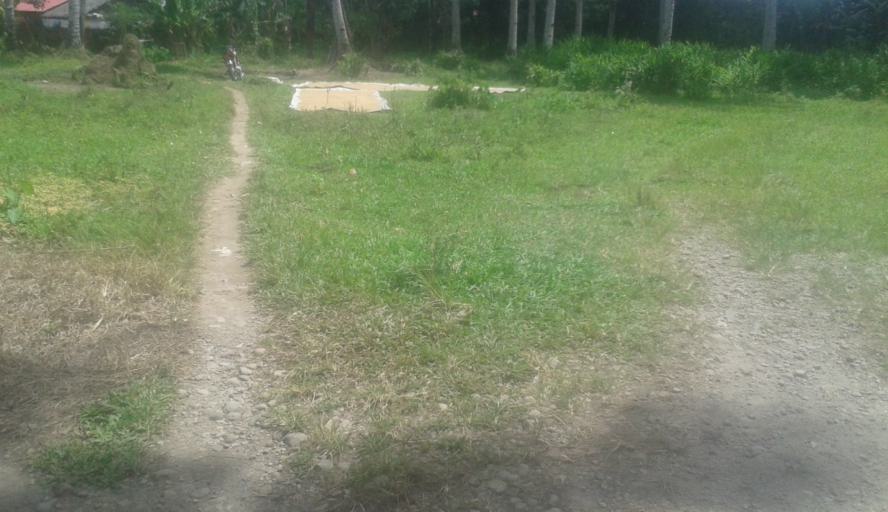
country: PH
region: Eastern Visayas
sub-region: Province of Leyte
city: Bugho
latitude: 10.8050
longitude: 124.9706
